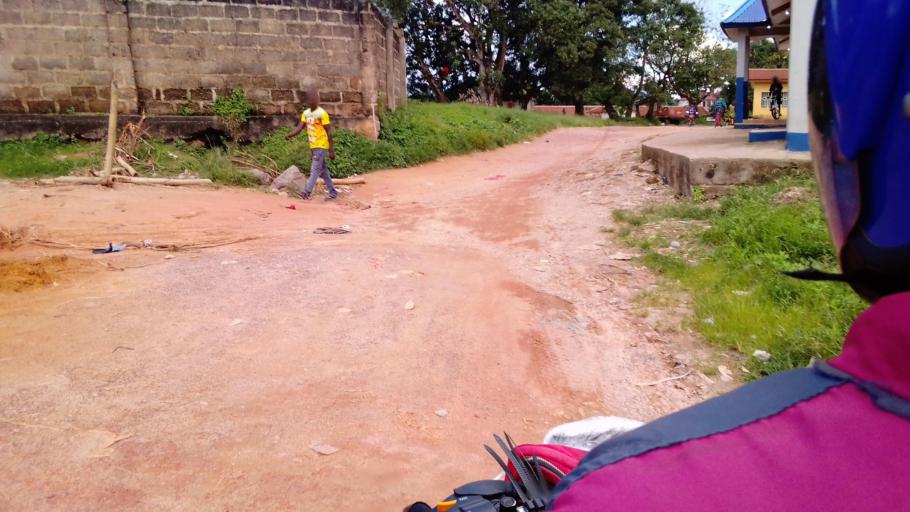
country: SL
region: Eastern Province
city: Koidu
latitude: 8.6485
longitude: -10.9722
